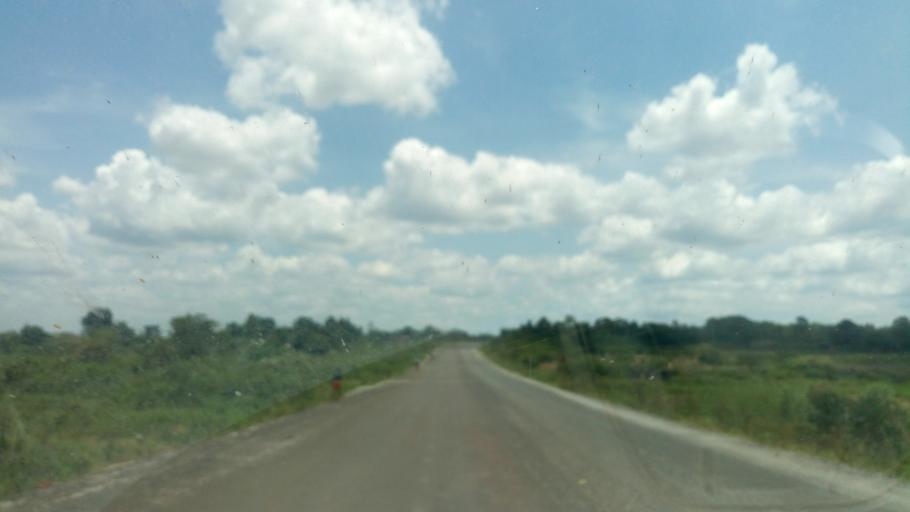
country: UG
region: Western Region
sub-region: Kiryandongo District
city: Kiryandongo
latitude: 1.7903
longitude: 31.9401
